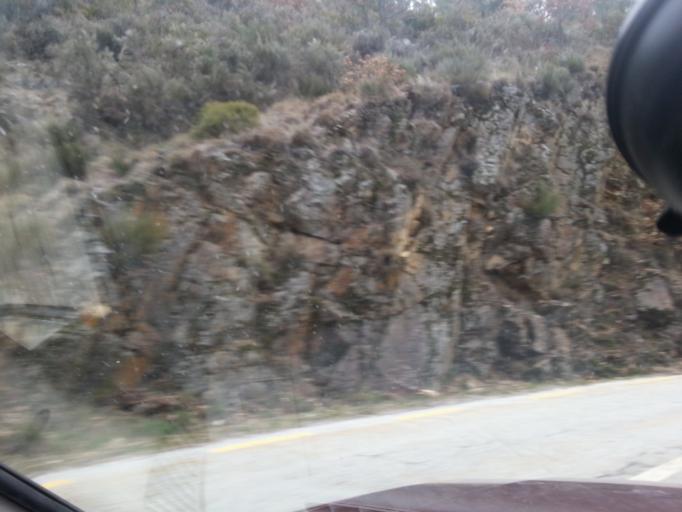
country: PT
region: Guarda
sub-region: Manteigas
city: Manteigas
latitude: 40.4125
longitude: -7.5537
